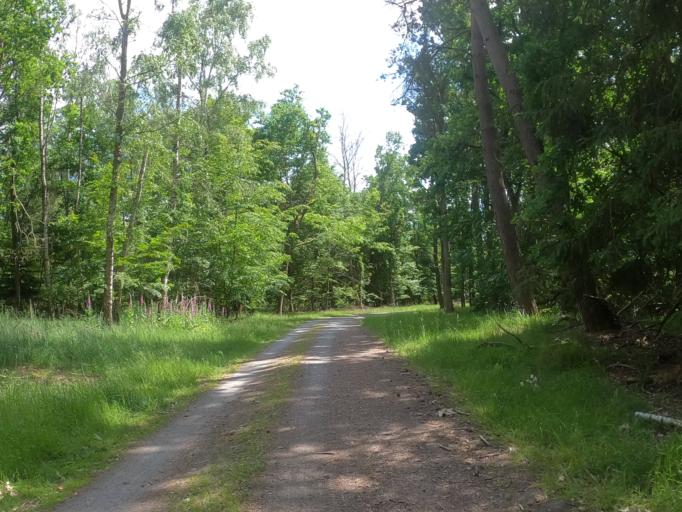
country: DE
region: Hesse
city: Morfelden-Walldorf
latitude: 49.9797
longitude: 8.5433
